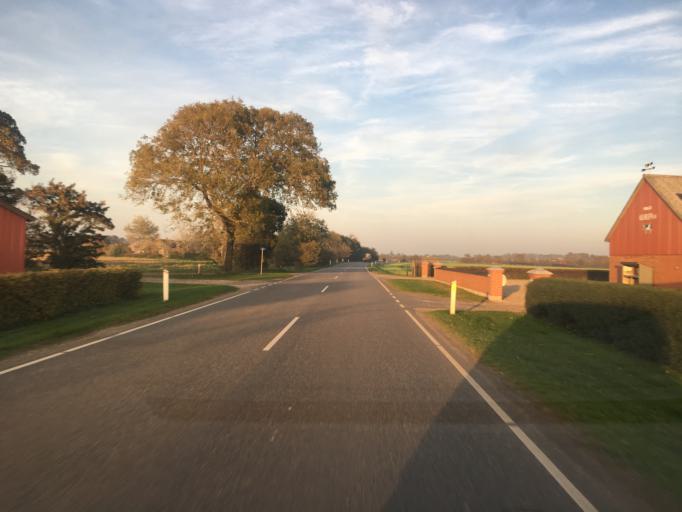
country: DK
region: South Denmark
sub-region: Tonder Kommune
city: Logumkloster
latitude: 55.0452
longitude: 9.0385
